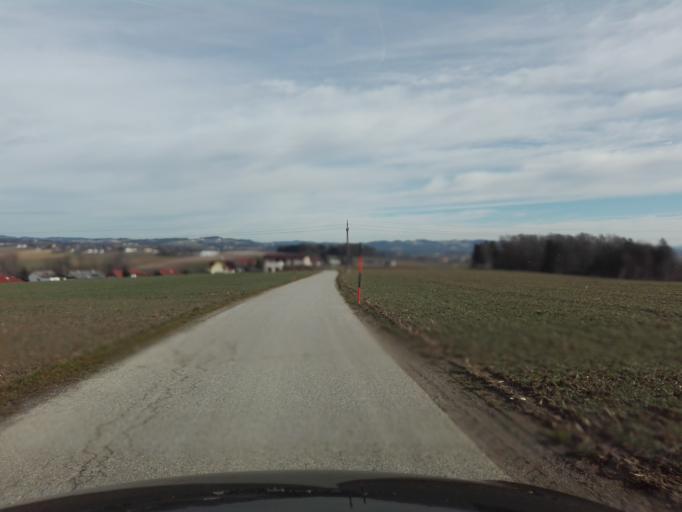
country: AT
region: Lower Austria
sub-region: Politischer Bezirk Amstetten
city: Ennsdorf
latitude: 48.2676
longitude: 14.5346
